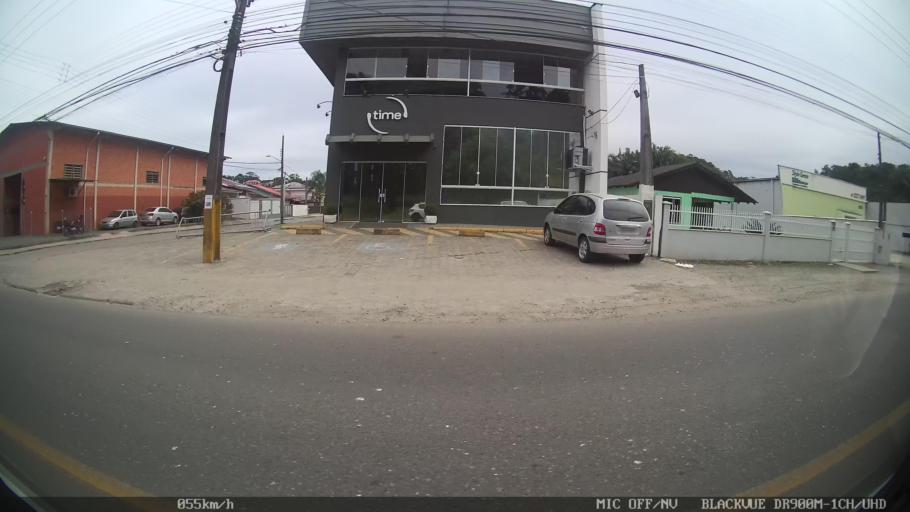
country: BR
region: Santa Catarina
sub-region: Joinville
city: Joinville
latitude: -26.3347
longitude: -48.8782
